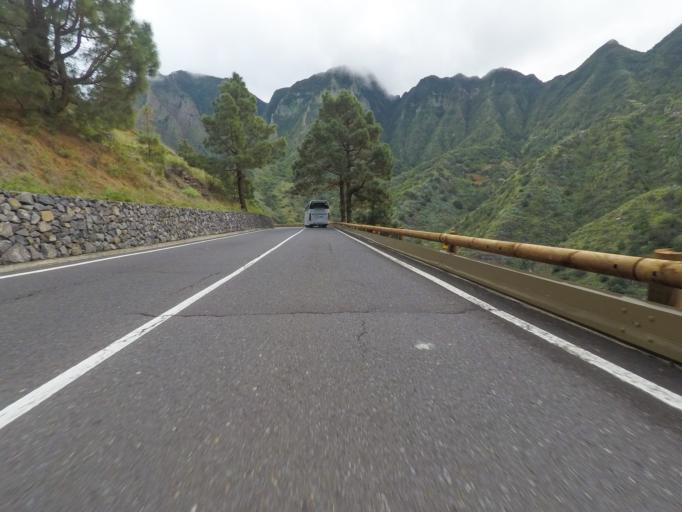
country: ES
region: Canary Islands
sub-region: Provincia de Santa Cruz de Tenerife
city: Hermigua
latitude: 28.1405
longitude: -17.1987
